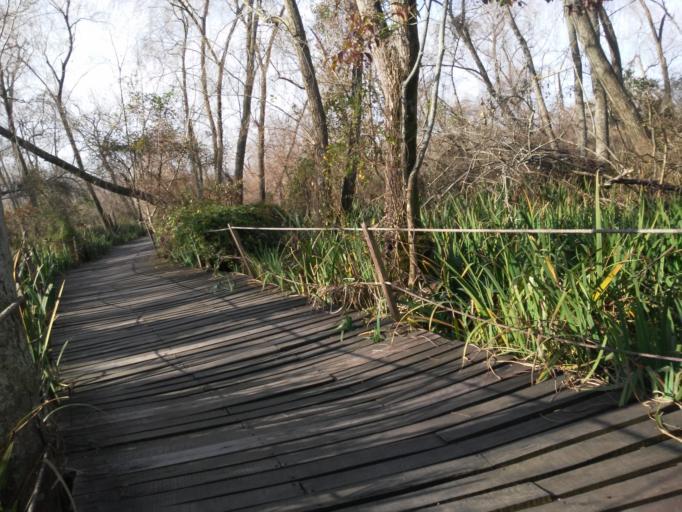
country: AR
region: Buenos Aires
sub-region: Partido de Avellaneda
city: Avellaneda
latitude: -34.6624
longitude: -58.3132
